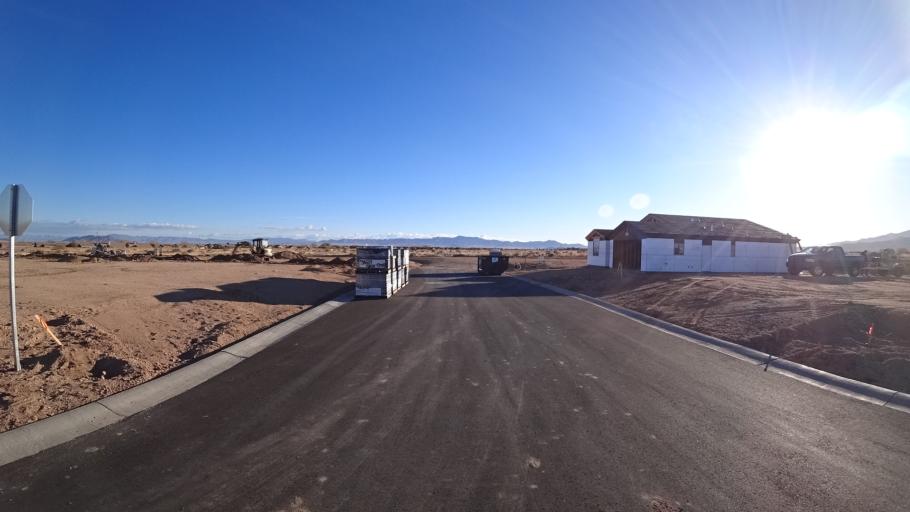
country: US
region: Arizona
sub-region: Mohave County
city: New Kingman-Butler
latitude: 35.2224
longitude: -113.9887
